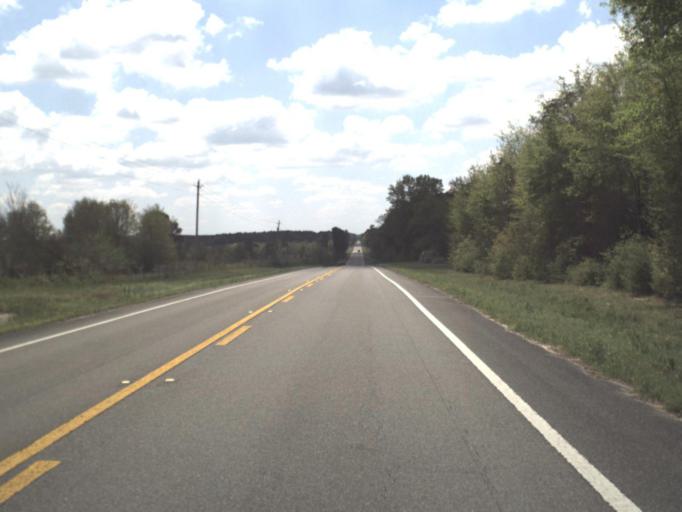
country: US
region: Florida
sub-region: Okaloosa County
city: Crestview
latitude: 30.9563
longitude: -86.6330
